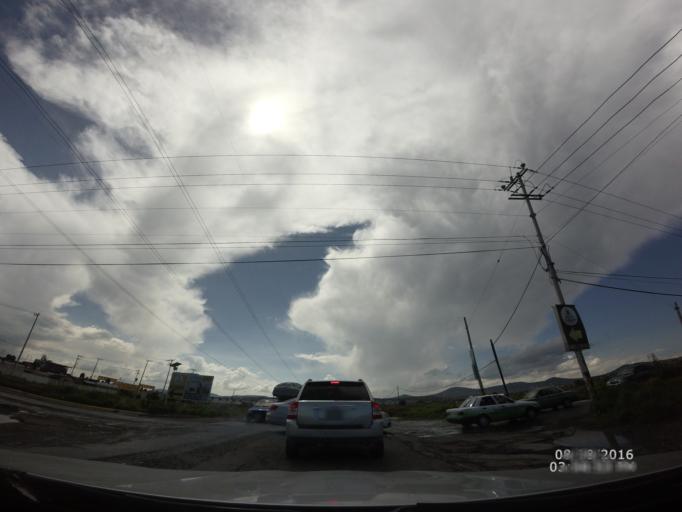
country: MX
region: Hidalgo
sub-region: Zempoala
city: Lindavista
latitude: 20.0376
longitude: -98.7815
